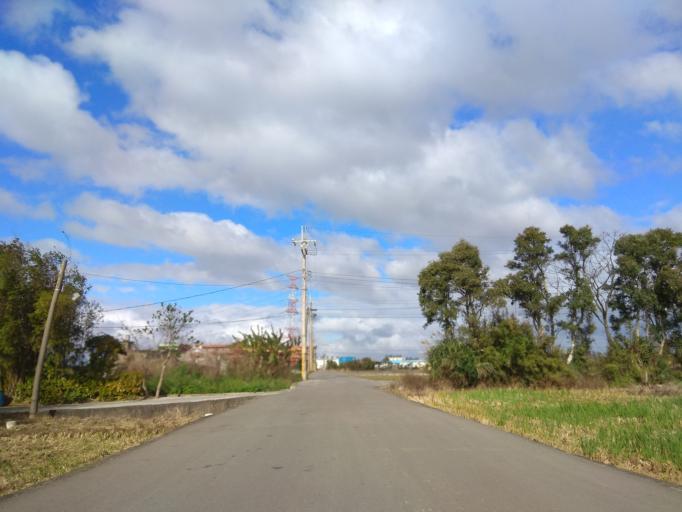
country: TW
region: Taiwan
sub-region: Hsinchu
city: Zhubei
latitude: 24.9735
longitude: 121.0705
